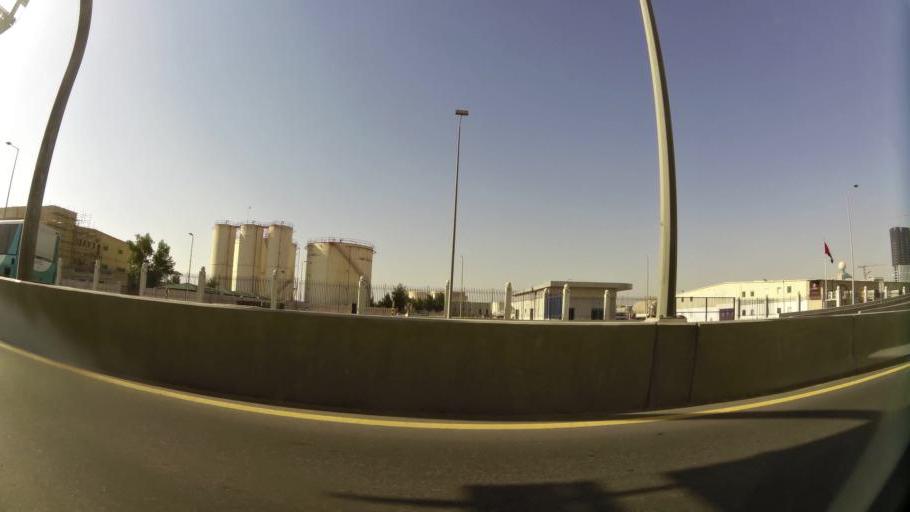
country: AE
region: Ajman
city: Ajman
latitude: 25.3939
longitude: 55.4674
